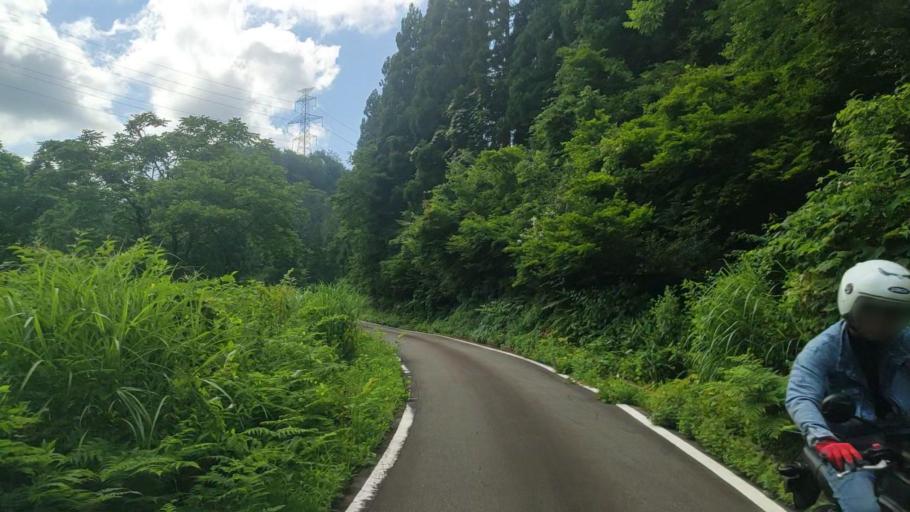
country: JP
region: Fukui
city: Katsuyama
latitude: 36.1730
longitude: 136.5237
